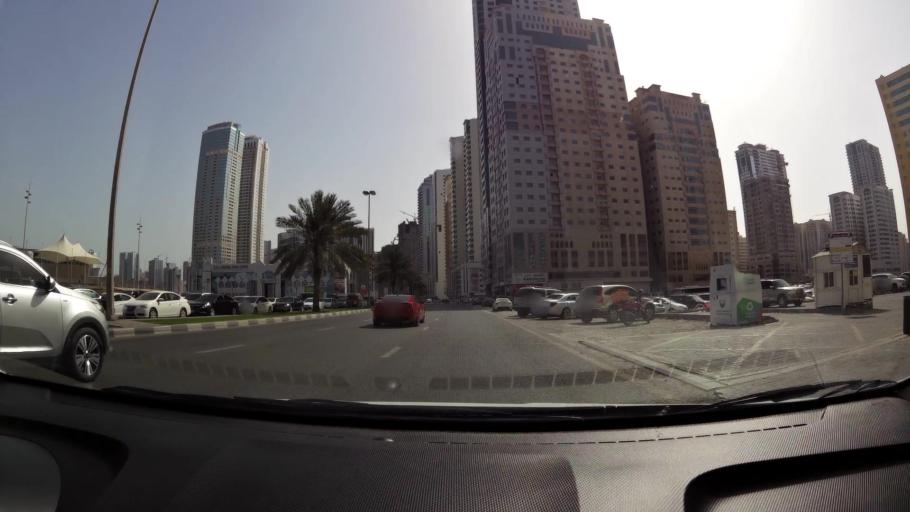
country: AE
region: Ash Shariqah
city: Sharjah
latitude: 25.3094
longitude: 55.3717
